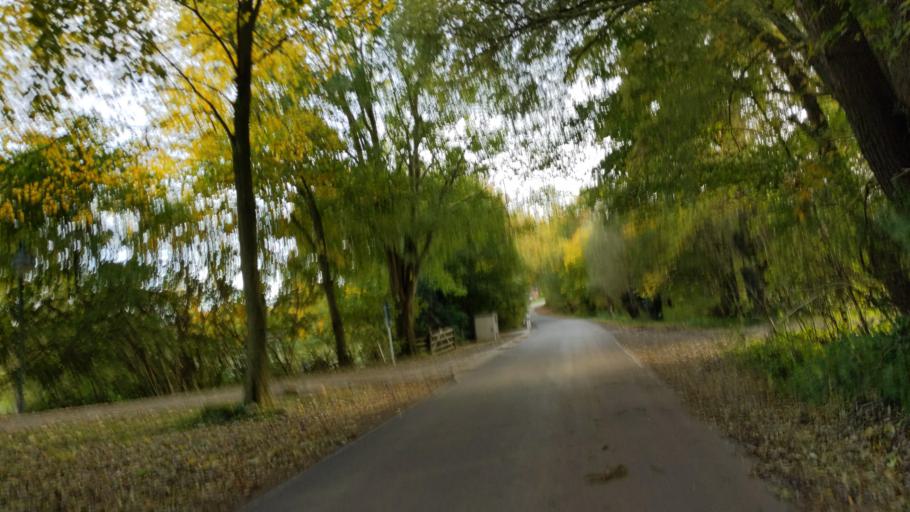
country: DE
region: Schleswig-Holstein
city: Susel
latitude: 54.1093
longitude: 10.7066
